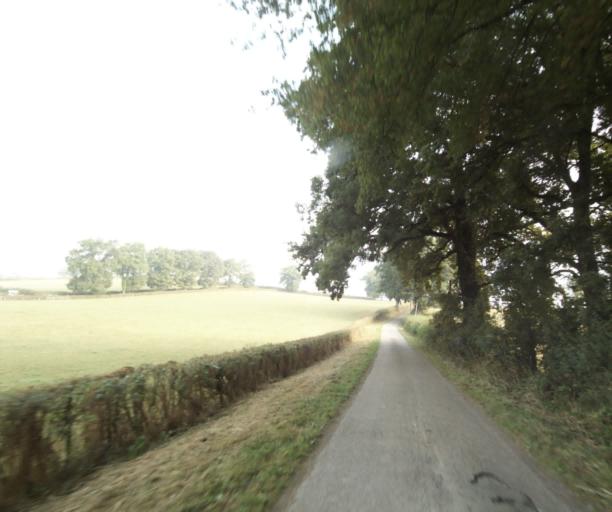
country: FR
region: Bourgogne
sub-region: Departement de Saone-et-Loire
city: Charolles
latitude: 46.4593
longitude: 4.2898
